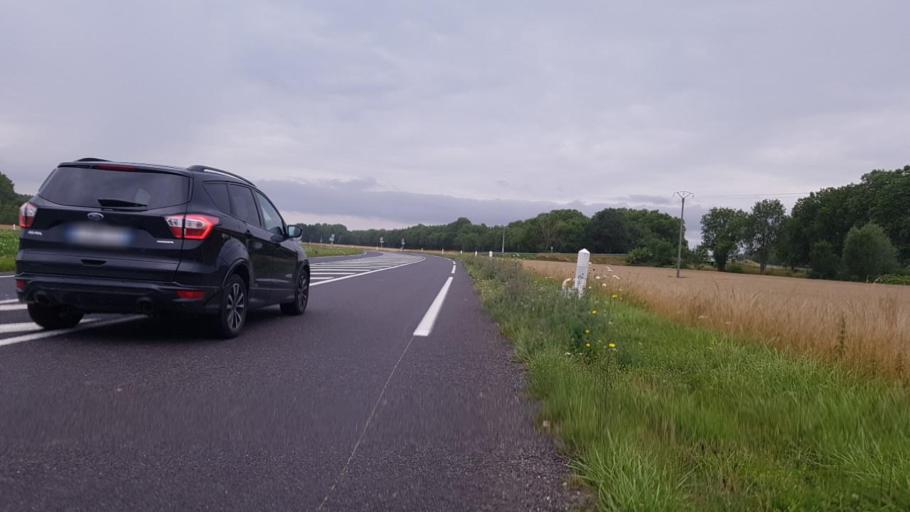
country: FR
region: Champagne-Ardenne
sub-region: Departement de la Marne
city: Pargny-sur-Saulx
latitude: 48.7550
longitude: 4.7147
